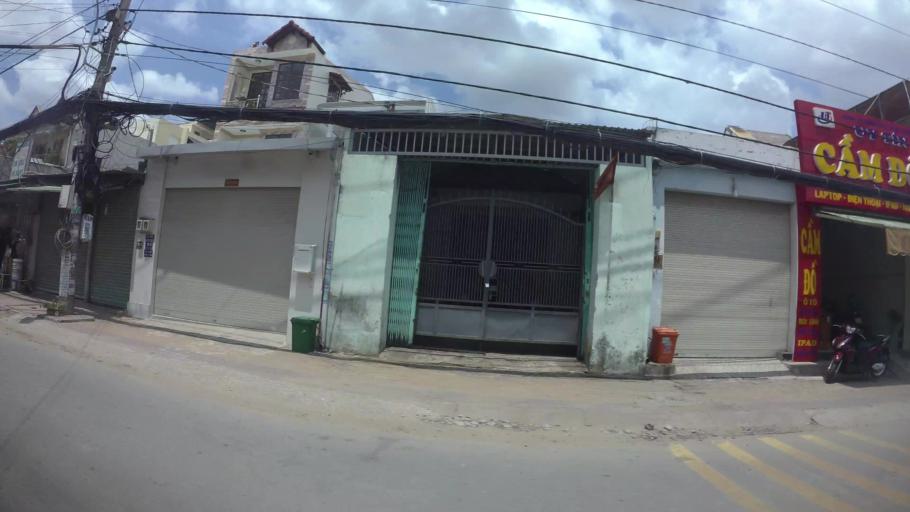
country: VN
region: Ho Chi Minh City
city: Quan Chin
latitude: 10.8382
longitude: 106.7809
